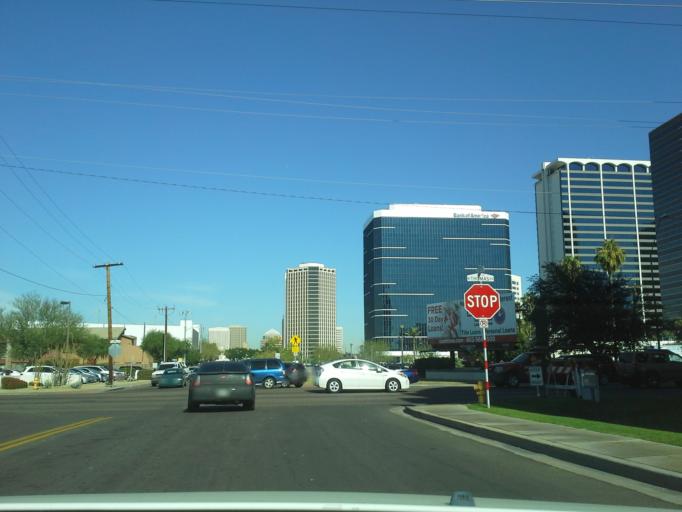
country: US
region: Arizona
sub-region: Maricopa County
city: Phoenix
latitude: 33.4799
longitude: -112.0750
